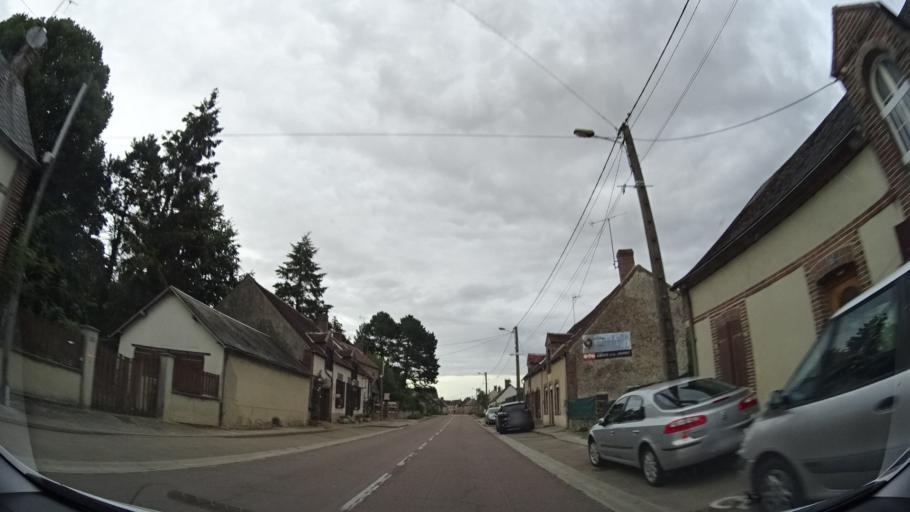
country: FR
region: Bourgogne
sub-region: Departement de l'Yonne
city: Charny
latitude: 47.9330
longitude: 3.1036
